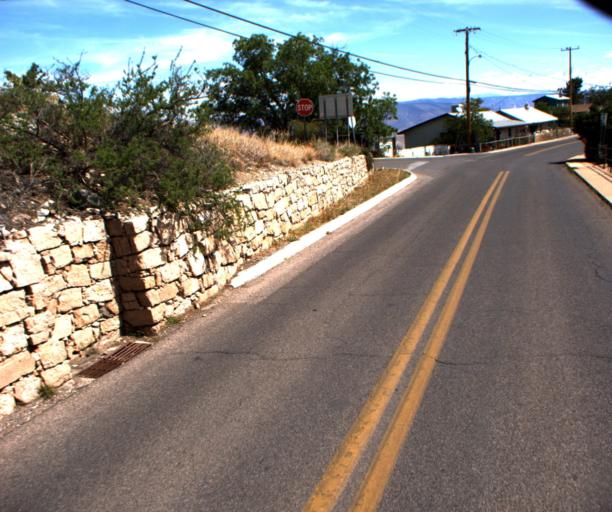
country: US
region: Arizona
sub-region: Yavapai County
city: Clarkdale
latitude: 34.7488
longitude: -112.1093
